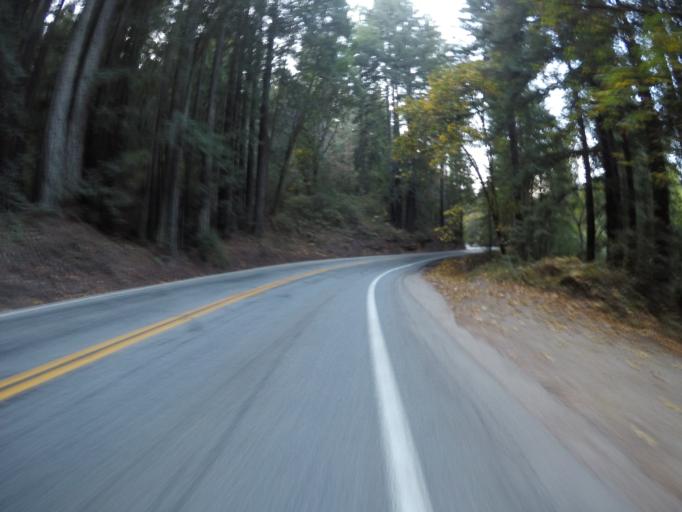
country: US
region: California
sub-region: Santa Cruz County
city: Pasatiempo
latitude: 37.0113
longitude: -122.0518
